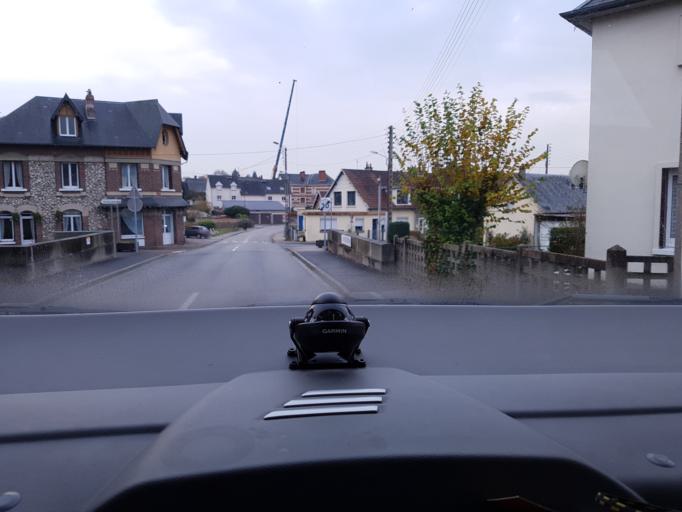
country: FR
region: Haute-Normandie
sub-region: Departement de la Seine-Maritime
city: Duclair
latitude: 49.4852
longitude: 0.8745
